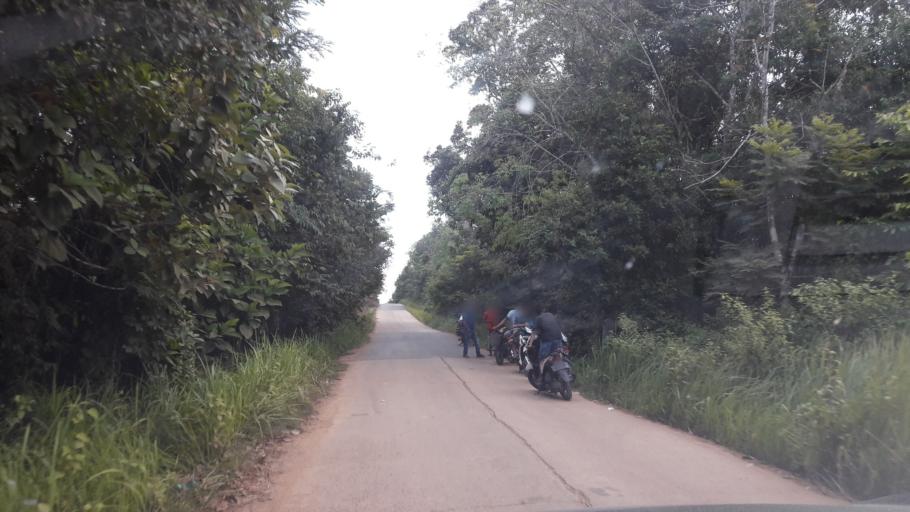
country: ID
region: South Sumatra
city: Gunungmenang
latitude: -3.2223
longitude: 103.8761
